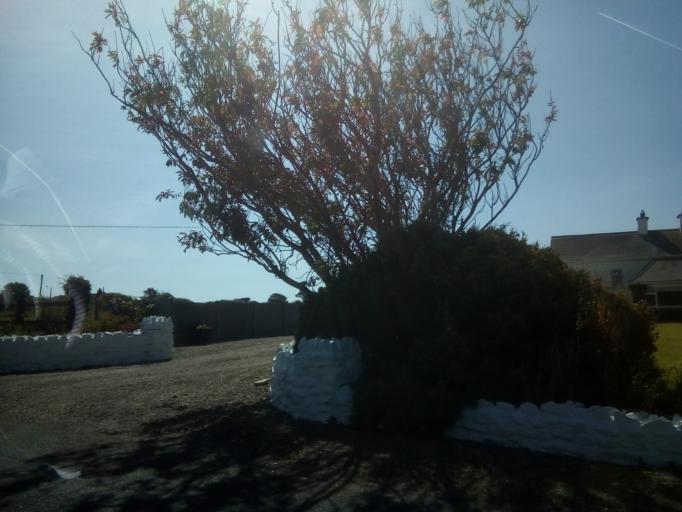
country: IE
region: Leinster
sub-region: Loch Garman
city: Loch Garman
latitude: 52.1847
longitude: -6.5774
